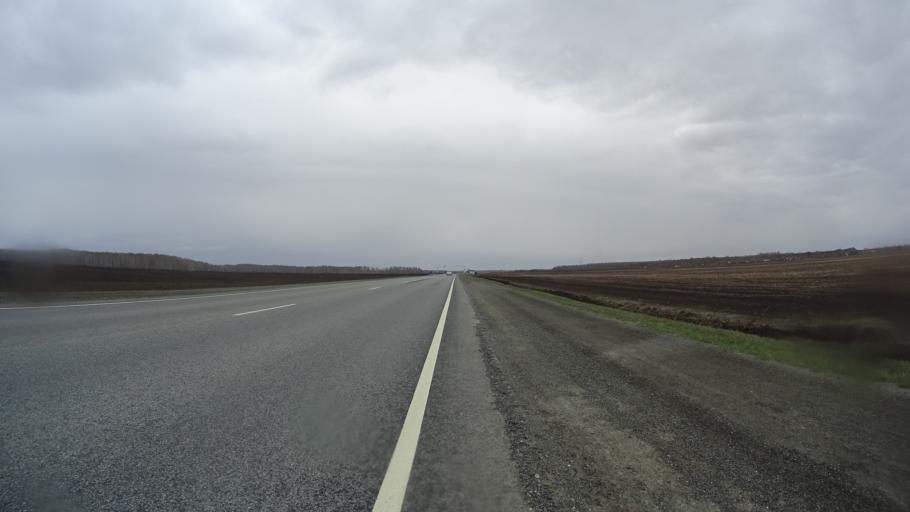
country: RU
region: Chelyabinsk
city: Krasnogorskiy
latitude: 54.5848
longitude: 61.2909
